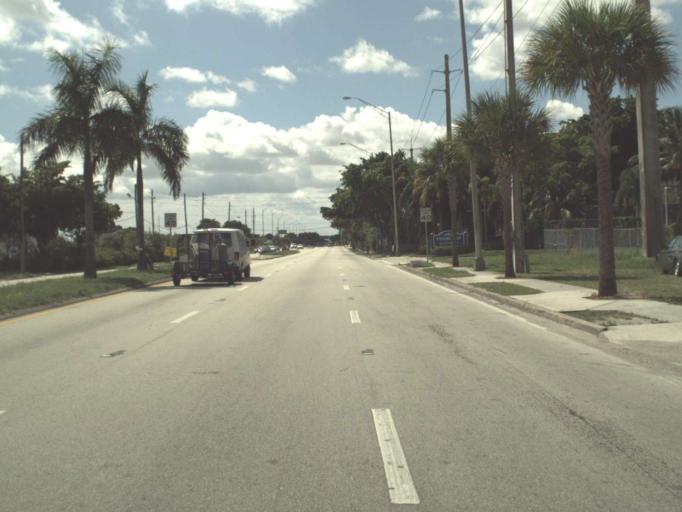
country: US
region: Florida
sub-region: Miami-Dade County
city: Golden Glades
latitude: 25.9200
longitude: -80.2121
